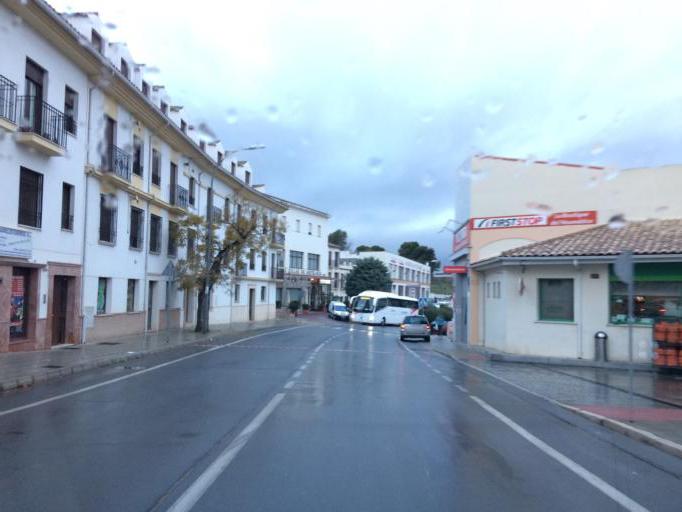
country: ES
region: Andalusia
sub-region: Provincia de Malaga
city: Antequera
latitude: 37.0234
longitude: -4.5601
